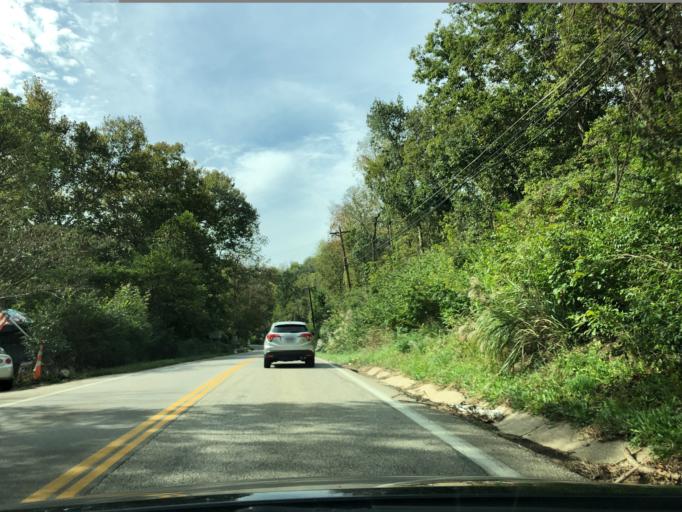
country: US
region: Ohio
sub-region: Clermont County
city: Milford
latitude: 39.1791
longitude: -84.2952
